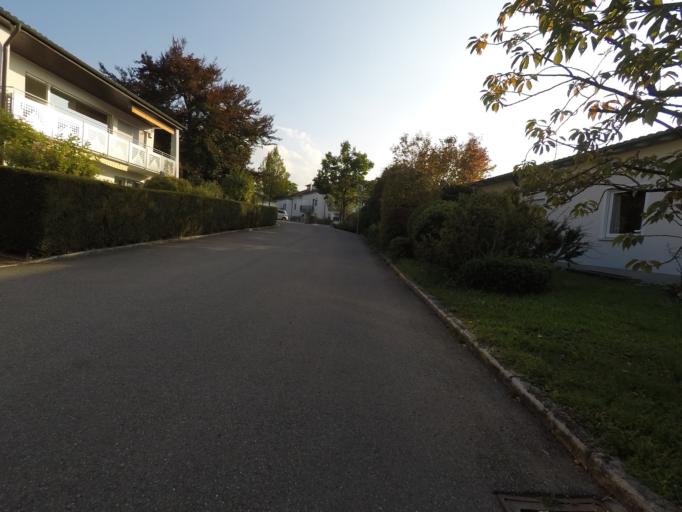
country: DE
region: Baden-Wuerttemberg
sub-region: Tuebingen Region
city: Pfullingen
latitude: 48.4683
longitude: 9.2357
